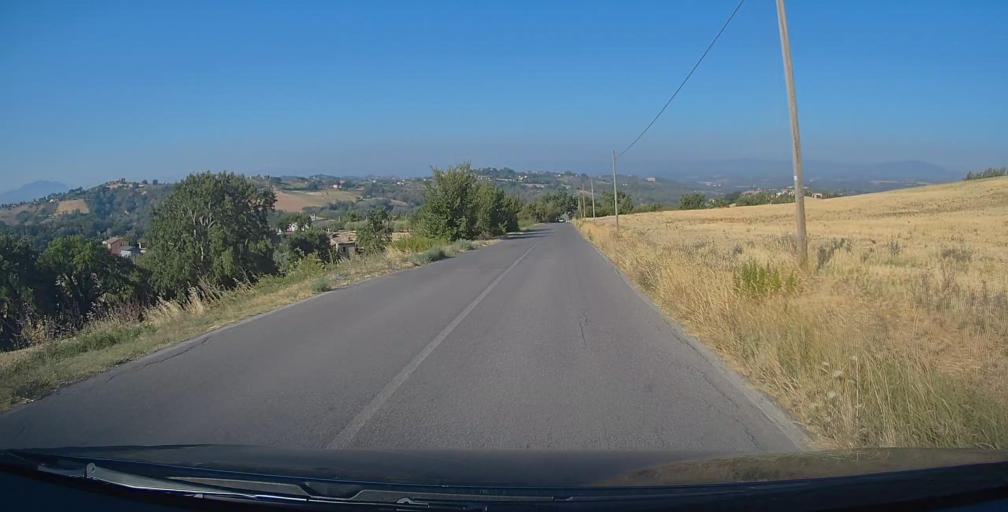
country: IT
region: Umbria
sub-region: Provincia di Terni
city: Calvi dell'Umbria
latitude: 42.4124
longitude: 12.5424
